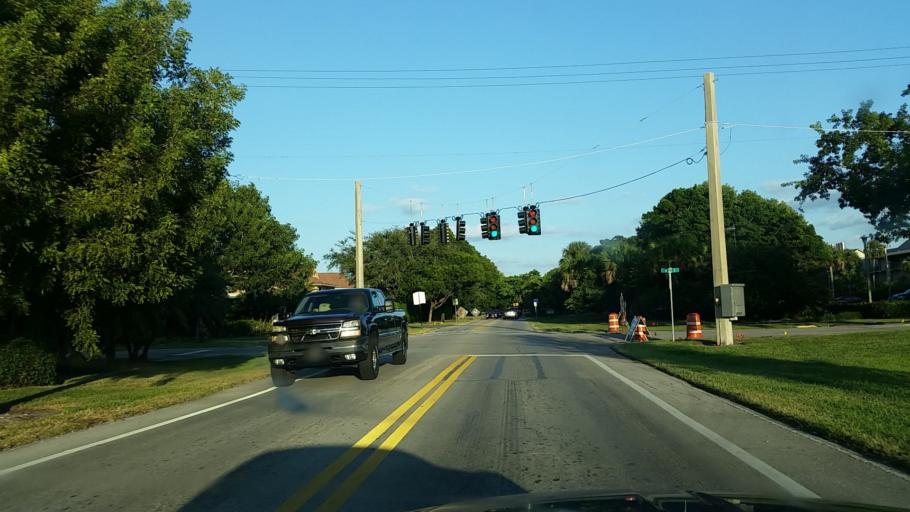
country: US
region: Florida
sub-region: Collier County
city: Naples
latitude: 26.1340
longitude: -81.7956
